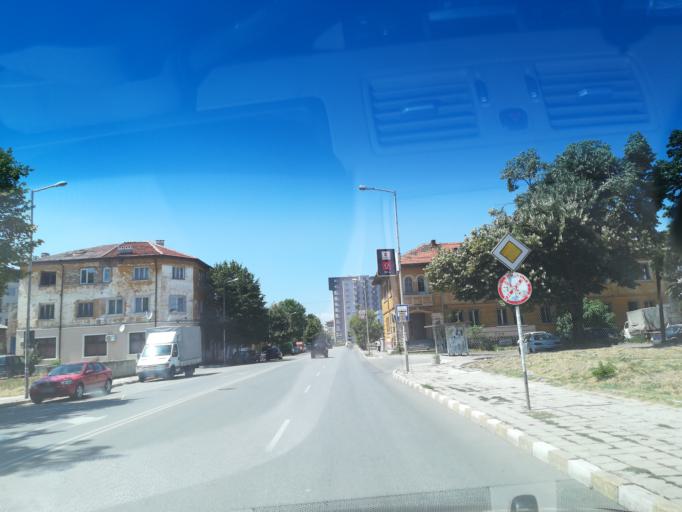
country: BG
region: Plovdiv
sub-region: Obshtina Asenovgrad
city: Asenovgrad
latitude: 42.0139
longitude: 24.8689
